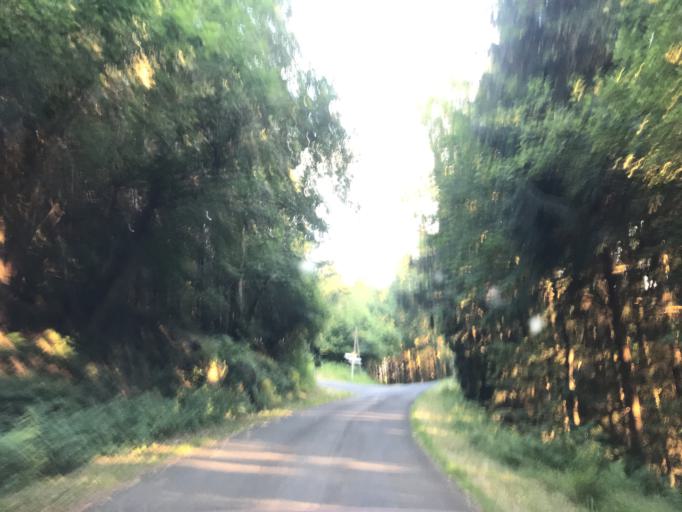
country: FR
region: Auvergne
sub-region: Departement du Puy-de-Dome
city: Courpiere
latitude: 45.7540
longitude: 3.6242
